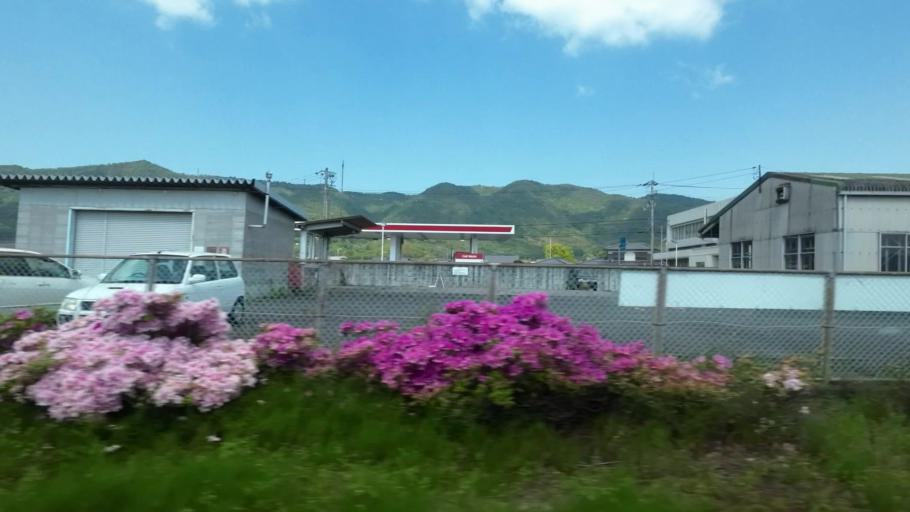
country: JP
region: Kagawa
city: Kan'onjicho
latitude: 34.1667
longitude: 133.6903
